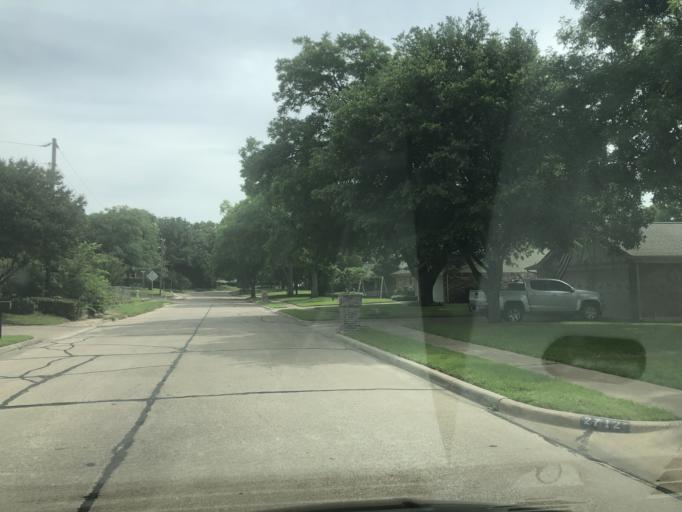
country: US
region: Texas
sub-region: Dallas County
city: Irving
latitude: 32.7959
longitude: -96.9830
